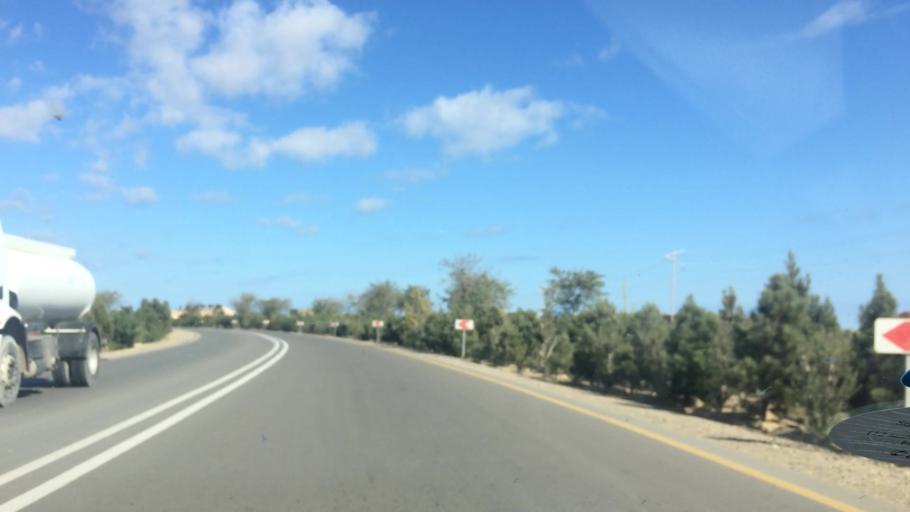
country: AZ
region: Baki
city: Pirallahi
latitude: 40.4226
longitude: 50.3565
